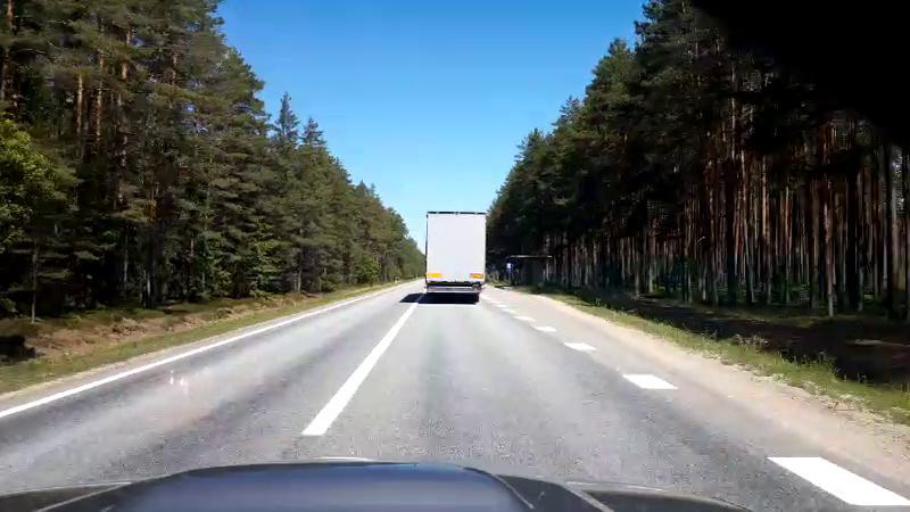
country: LV
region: Salacgrivas
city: Salacgriva
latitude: 57.5424
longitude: 24.4320
